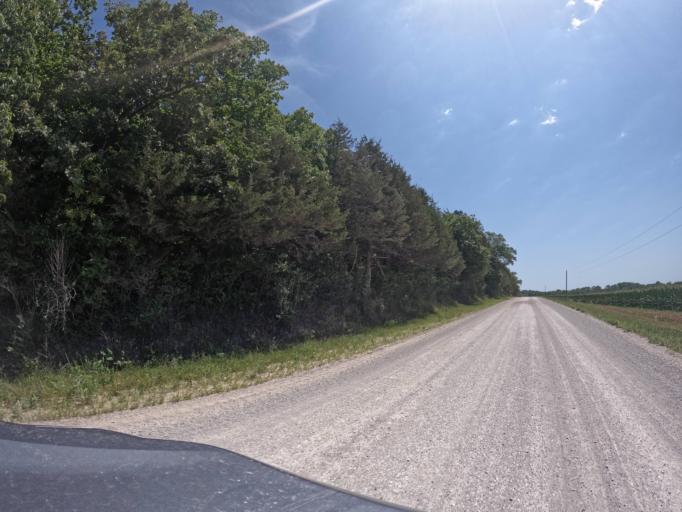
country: US
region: Iowa
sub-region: Henry County
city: Mount Pleasant
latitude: 40.8909
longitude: -91.5426
